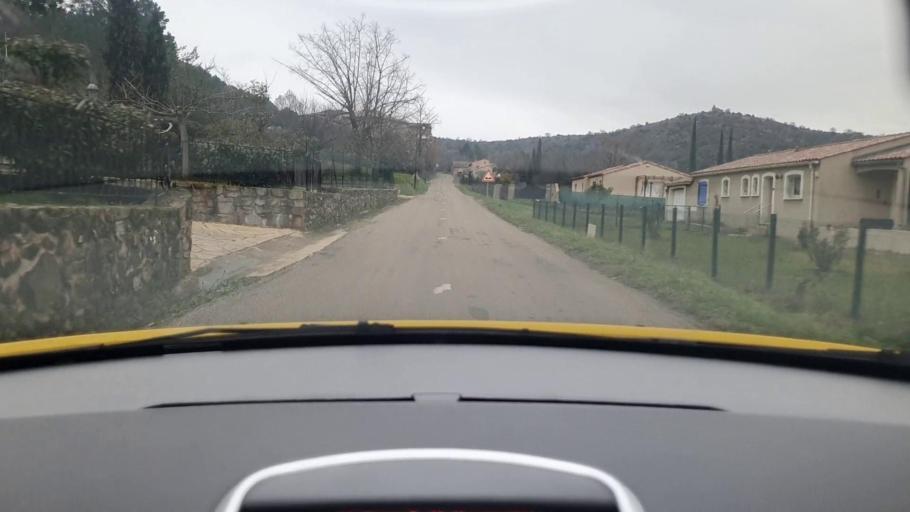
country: FR
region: Languedoc-Roussillon
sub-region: Departement du Gard
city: Molieres-sur-Ceze
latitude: 44.3036
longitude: 4.1490
